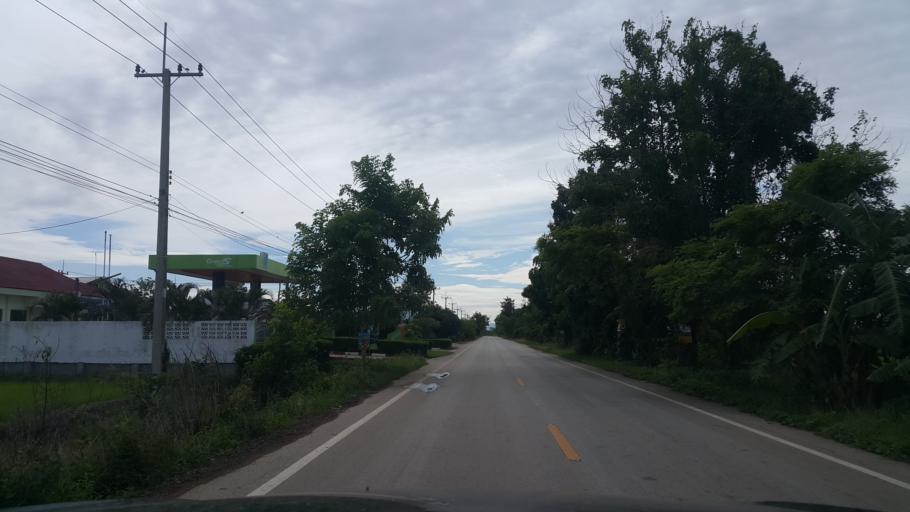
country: TH
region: Uttaradit
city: Phichai
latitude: 17.2853
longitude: 100.0232
